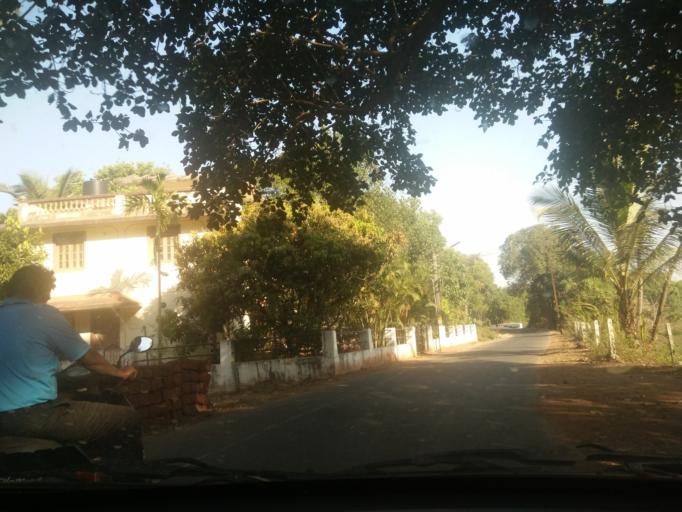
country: IN
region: Goa
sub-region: South Goa
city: Colva
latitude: 15.3043
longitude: 73.9133
